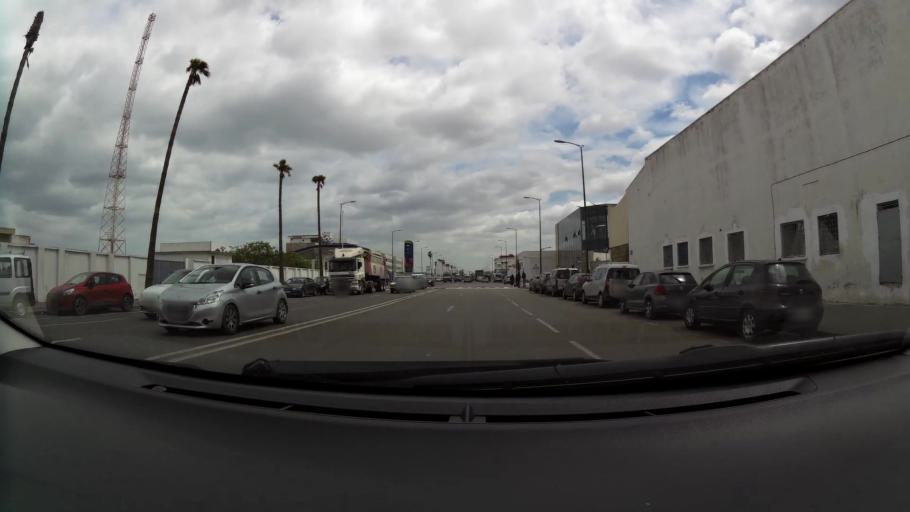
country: MA
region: Grand Casablanca
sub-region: Casablanca
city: Casablanca
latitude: 33.6102
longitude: -7.5642
